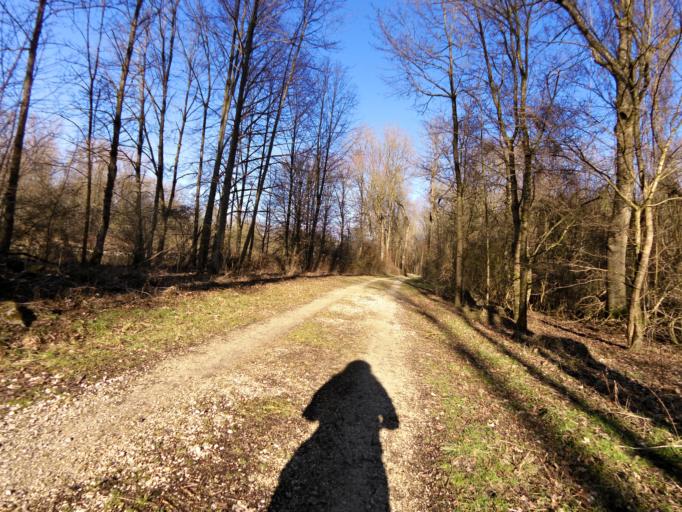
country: DE
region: Bavaria
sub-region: Lower Bavaria
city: Eching
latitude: 48.5124
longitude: 12.0790
